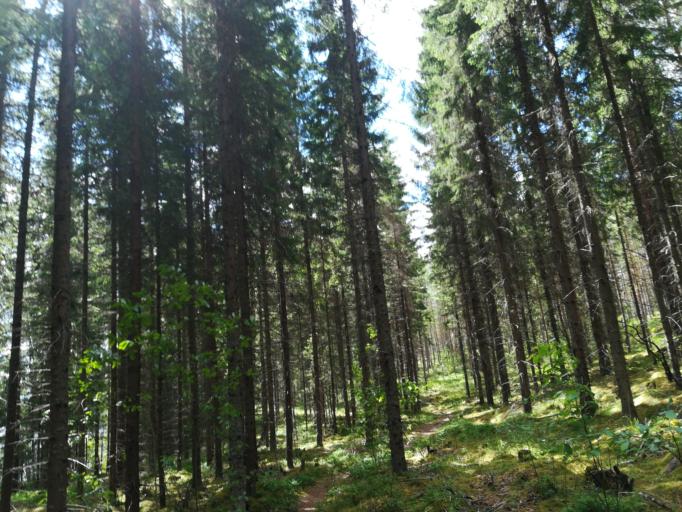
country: FI
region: Southern Savonia
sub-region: Mikkeli
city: Maentyharju
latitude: 61.3642
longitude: 26.9340
